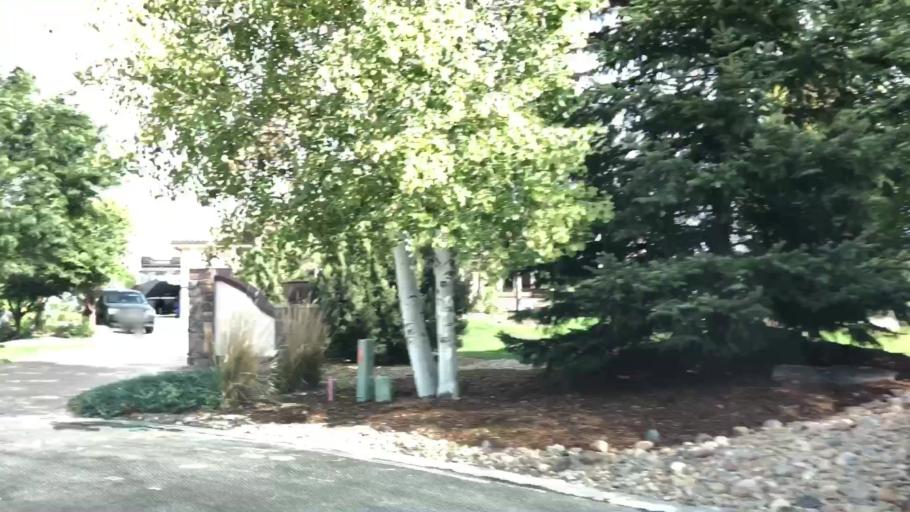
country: US
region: Colorado
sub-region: Larimer County
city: Loveland
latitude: 40.4397
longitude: -105.0551
